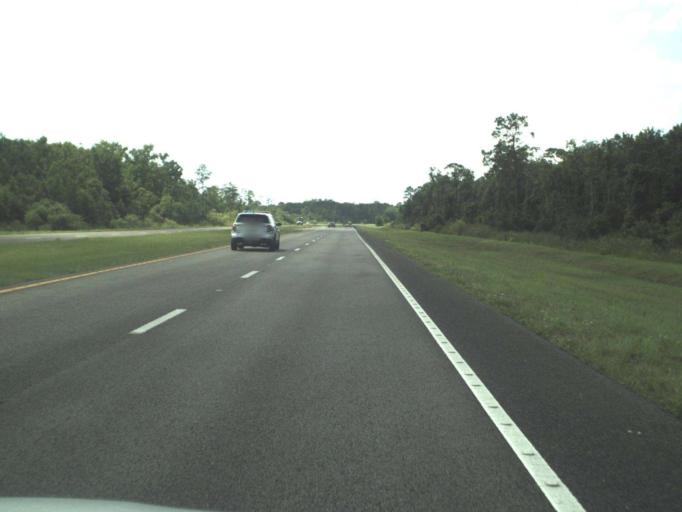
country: US
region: Florida
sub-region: Brevard County
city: Cocoa West
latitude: 28.3872
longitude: -80.9323
